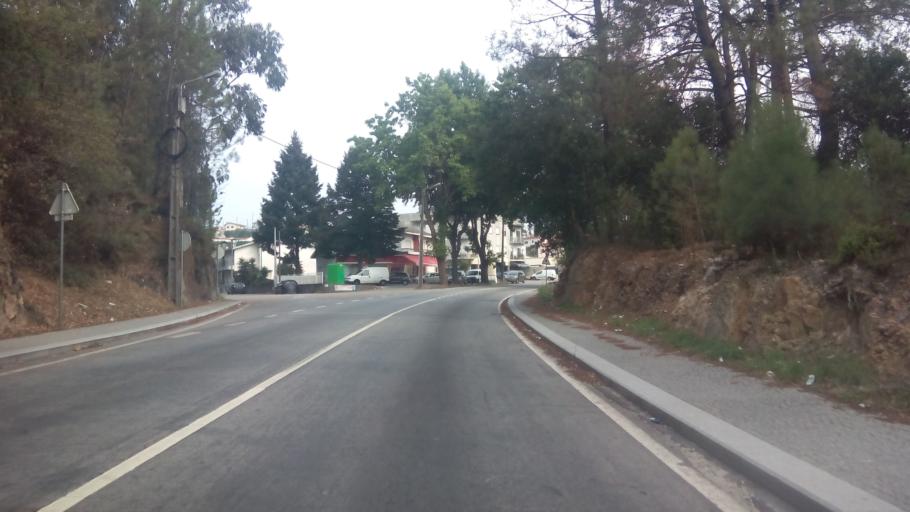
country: PT
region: Porto
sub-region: Paredes
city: Gandra
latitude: 41.1869
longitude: -8.4373
